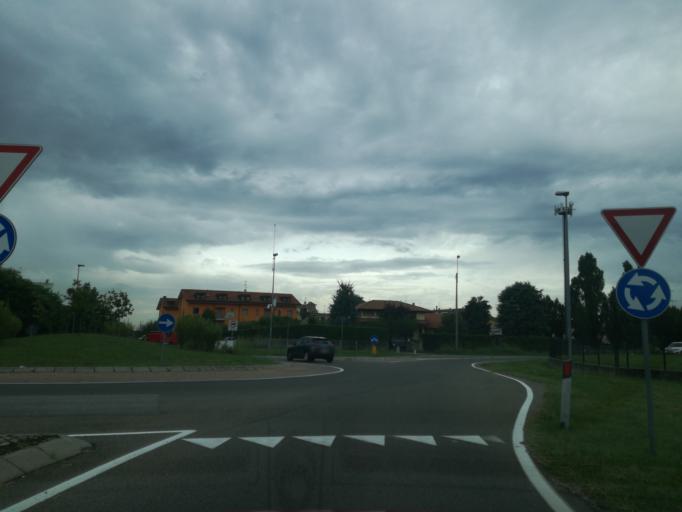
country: IT
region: Lombardy
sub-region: Provincia di Monza e Brianza
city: Mezzago
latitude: 45.6278
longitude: 9.4378
